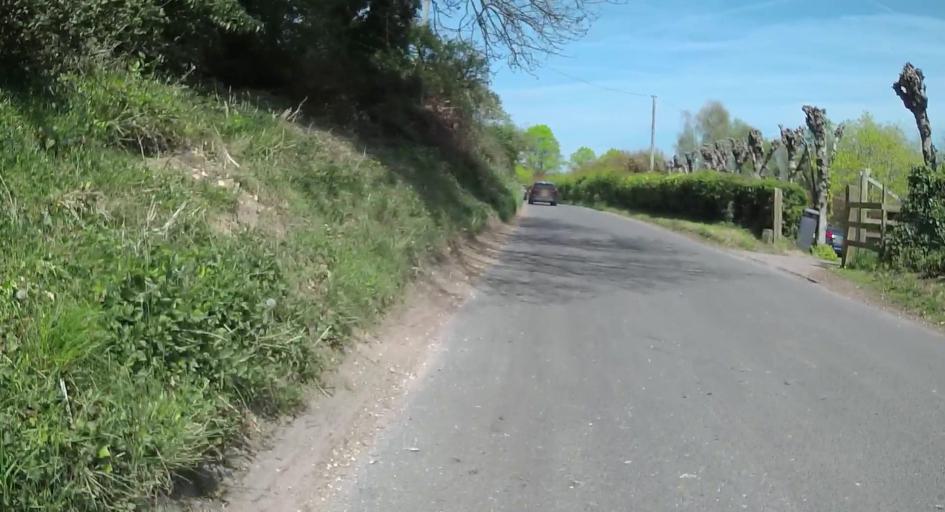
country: GB
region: England
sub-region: Hampshire
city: Abbotts Ann
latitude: 51.1208
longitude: -1.4964
